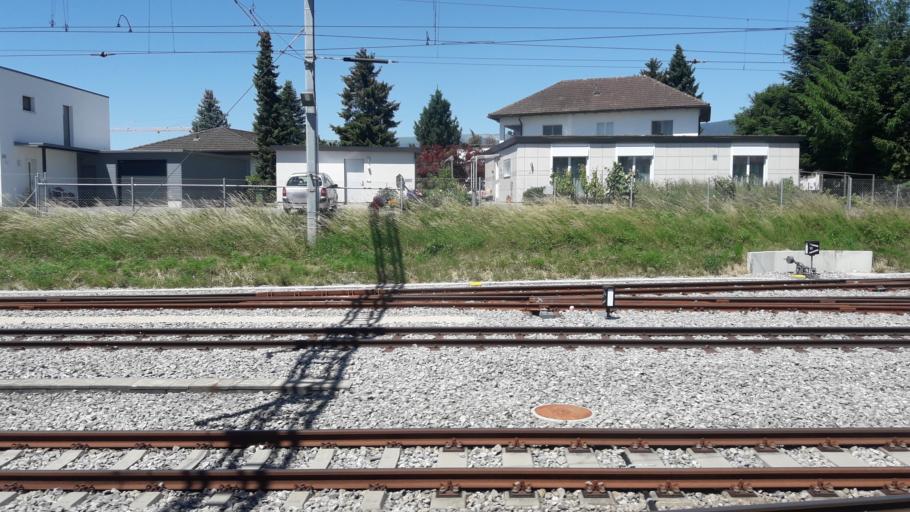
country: CH
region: Bern
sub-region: Seeland District
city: Tauffelen
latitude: 47.0659
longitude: 7.1978
